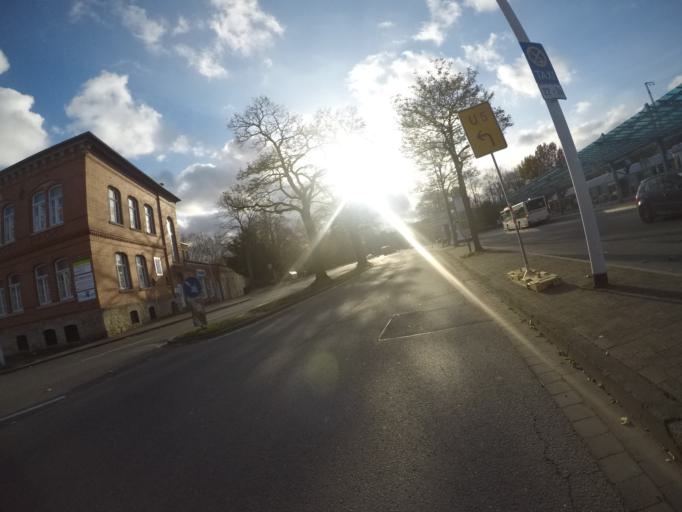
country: DE
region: North Rhine-Westphalia
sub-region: Regierungsbezirk Detmold
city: Herford
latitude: 52.1188
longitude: 8.6645
